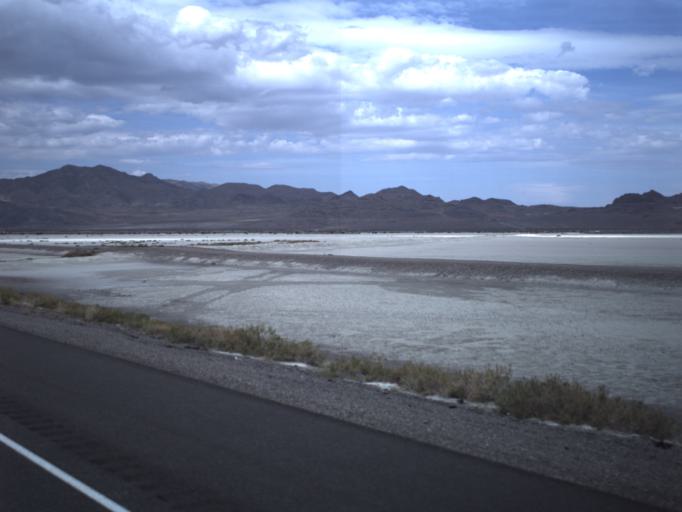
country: US
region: Utah
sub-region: Tooele County
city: Wendover
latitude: 40.7413
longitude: -113.9499
